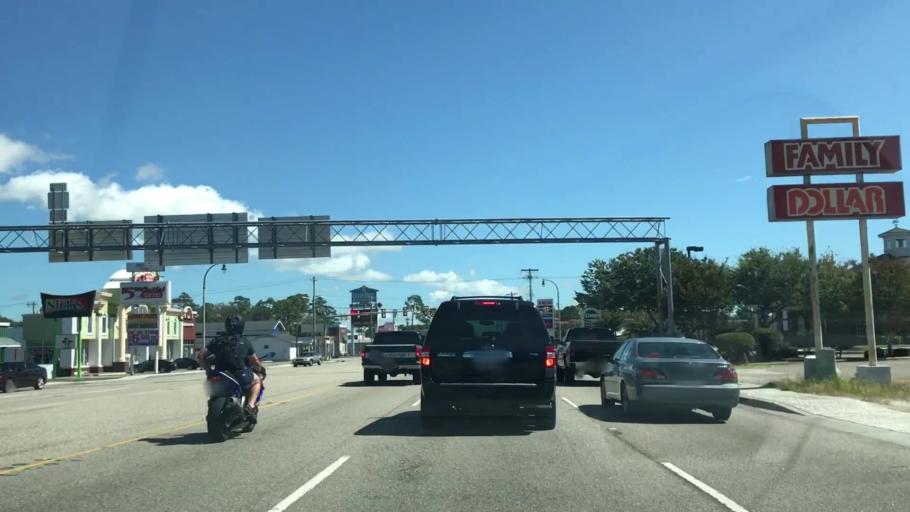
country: US
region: South Carolina
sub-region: Horry County
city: North Myrtle Beach
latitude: 33.8290
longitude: -78.6790
